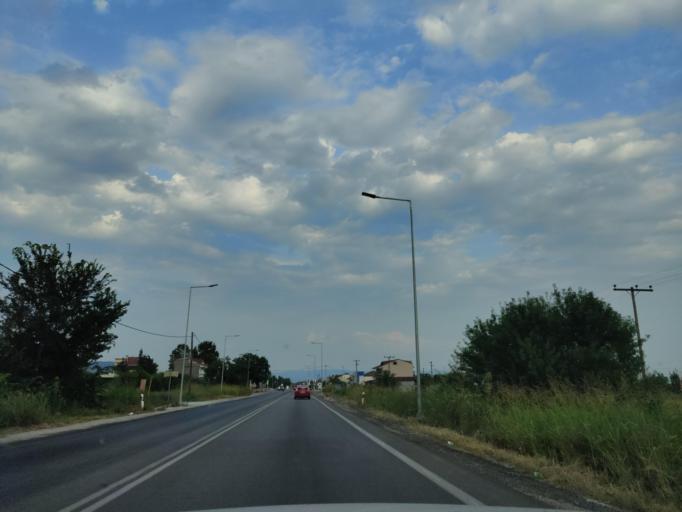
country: GR
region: East Macedonia and Thrace
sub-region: Nomos Dramas
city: Xiropotamos
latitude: 41.1574
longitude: 24.1004
